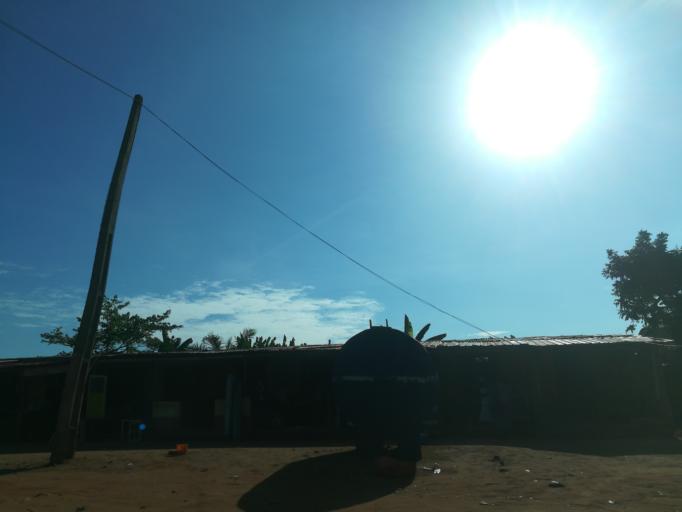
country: NG
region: Lagos
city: Ikorodu
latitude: 6.5680
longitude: 3.5338
